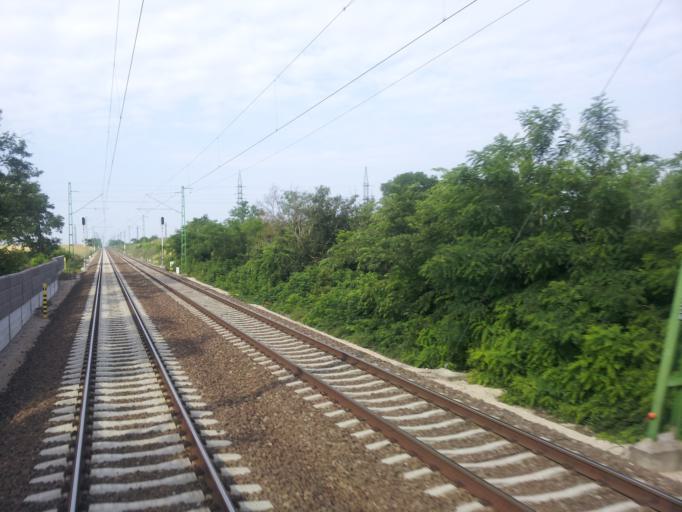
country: HU
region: Fejer
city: Baracska
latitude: 47.2910
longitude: 18.7463
